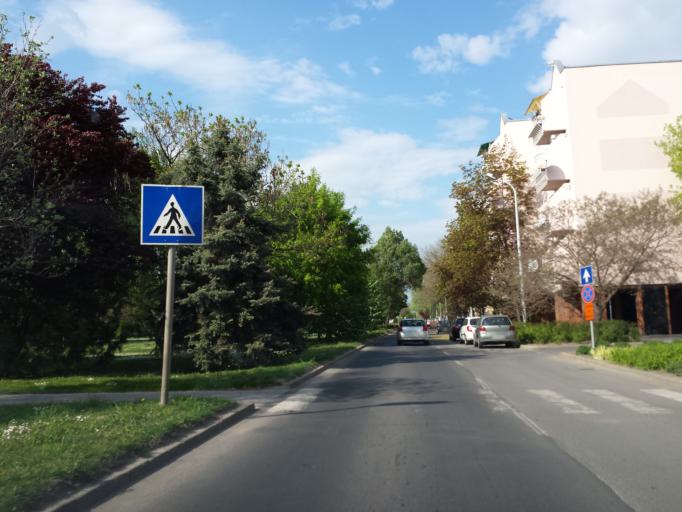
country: HU
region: Csongrad
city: Mako
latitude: 46.2170
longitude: 20.4758
